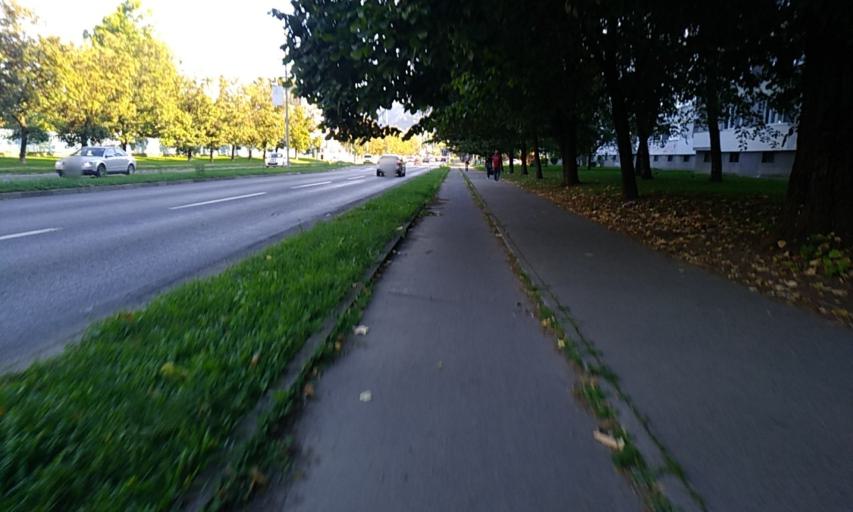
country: BA
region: Republika Srpska
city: Starcevica
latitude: 44.7734
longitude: 17.2082
